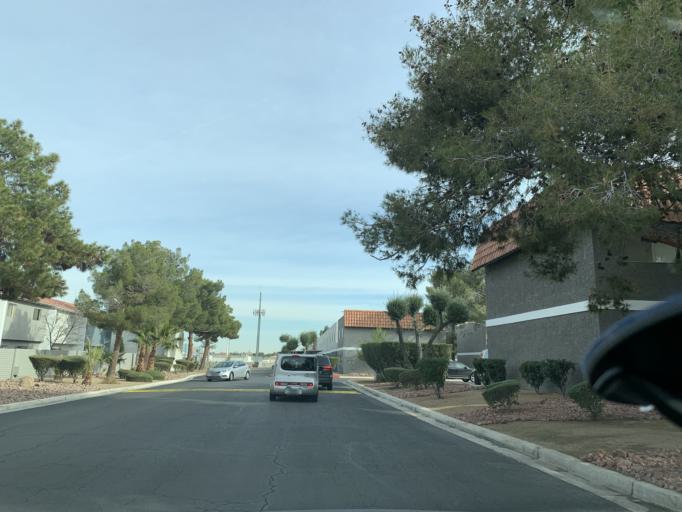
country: US
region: Nevada
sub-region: Clark County
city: Spring Valley
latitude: 36.0984
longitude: -115.2293
